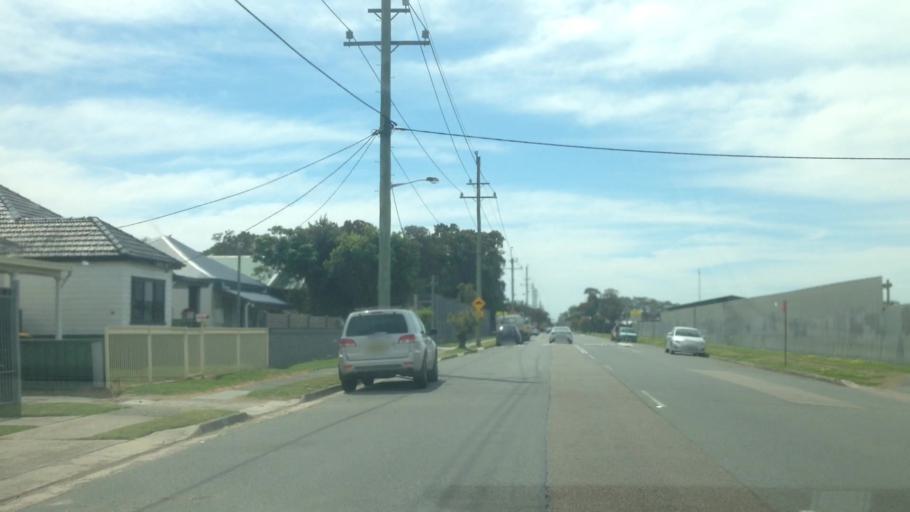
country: AU
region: New South Wales
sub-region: Newcastle
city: Broadmeadow
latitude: -32.9315
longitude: 151.7360
